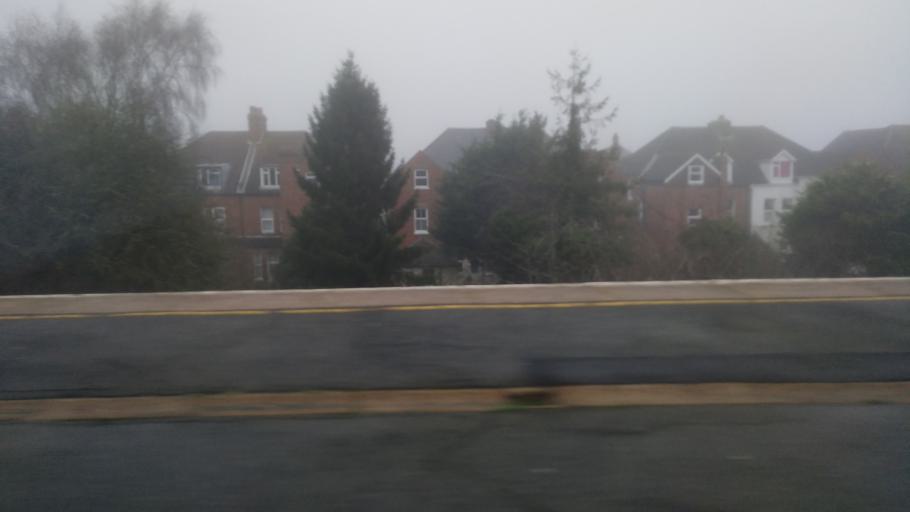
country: GB
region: England
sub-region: Kent
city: Folkestone
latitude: 51.0829
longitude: 1.1665
